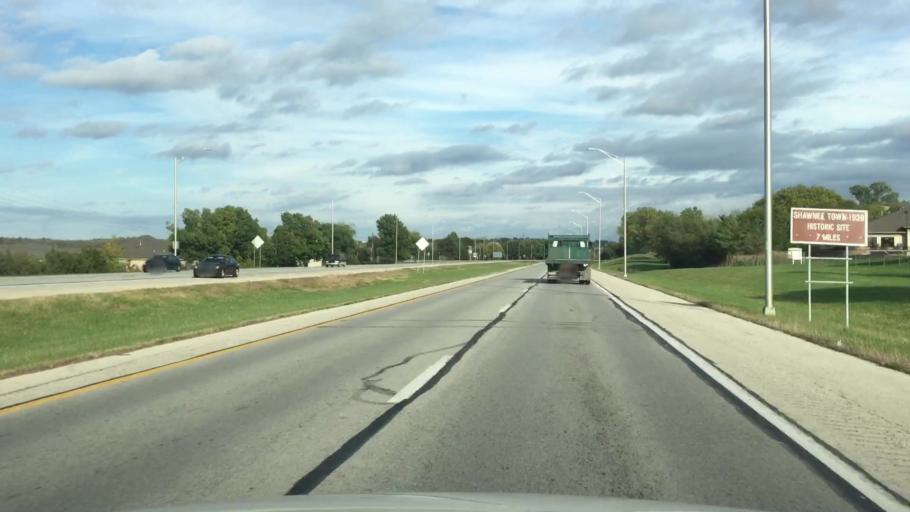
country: US
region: Kansas
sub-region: Wyandotte County
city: Edwardsville
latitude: 39.0083
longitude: -94.8378
